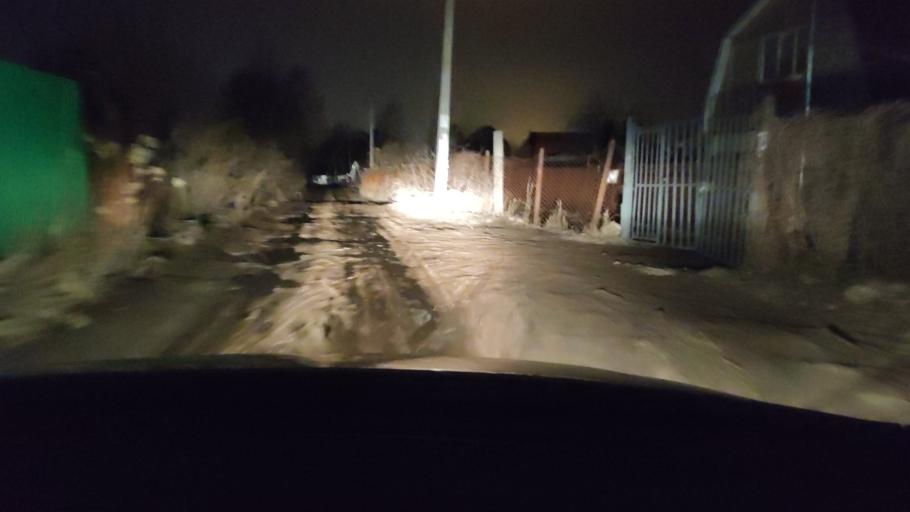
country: RU
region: Tatarstan
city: Vysokaya Gora
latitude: 55.8345
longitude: 49.2250
